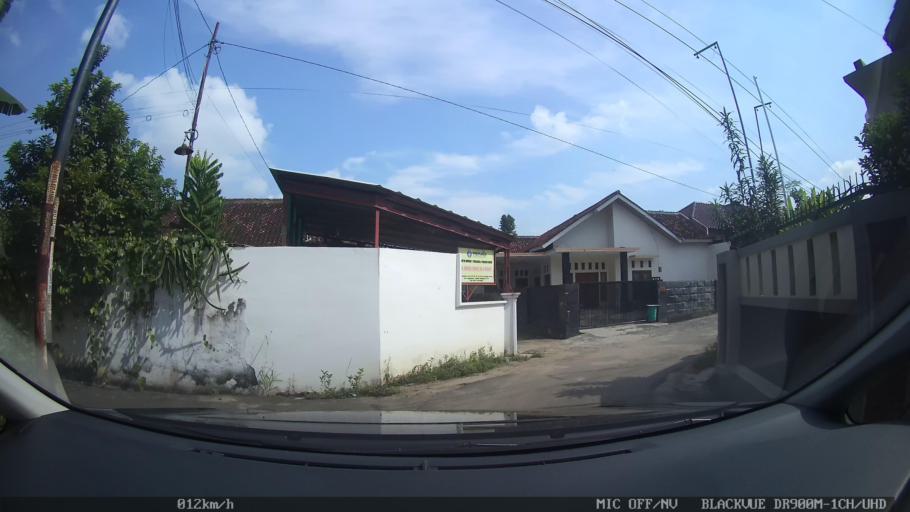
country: ID
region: Lampung
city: Kedaton
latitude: -5.3832
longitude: 105.2411
